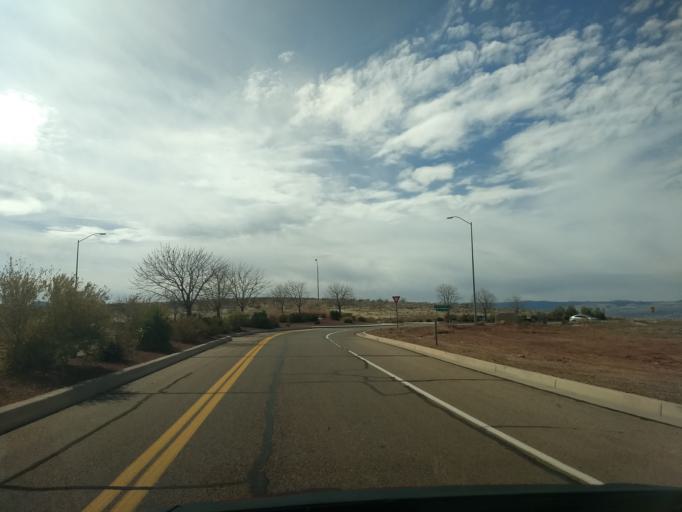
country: US
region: Utah
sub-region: Washington County
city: Washington
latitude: 37.0252
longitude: -113.5081
